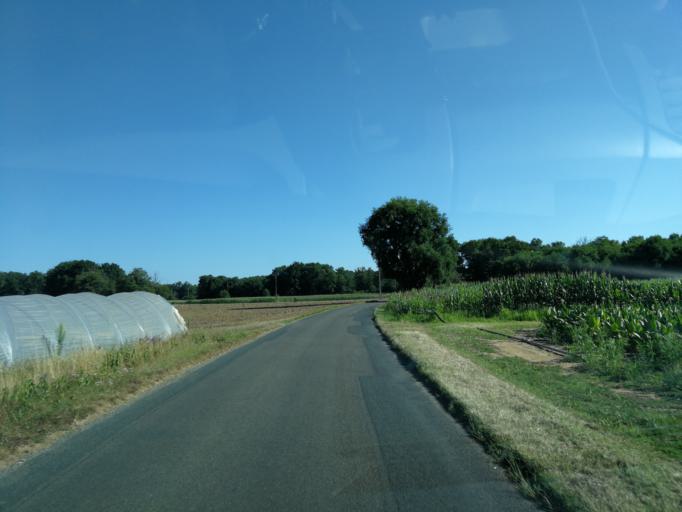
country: FR
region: Midi-Pyrenees
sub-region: Departement du Lot
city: Gourdon
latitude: 44.7896
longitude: 1.3691
